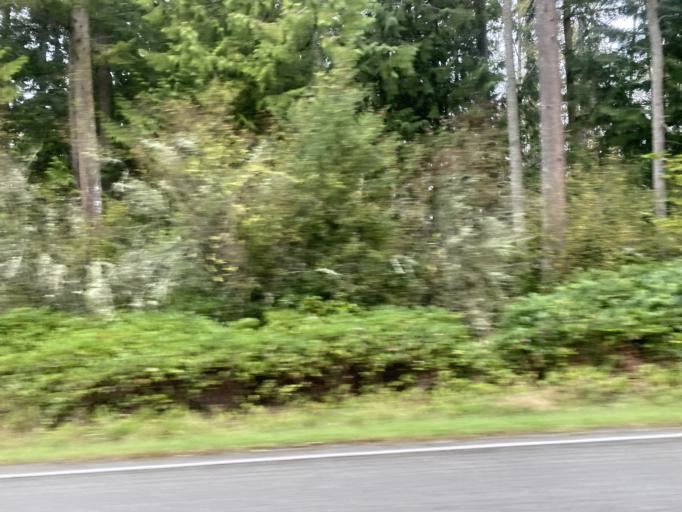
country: US
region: Washington
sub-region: Island County
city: Freeland
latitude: 48.0819
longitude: -122.4923
